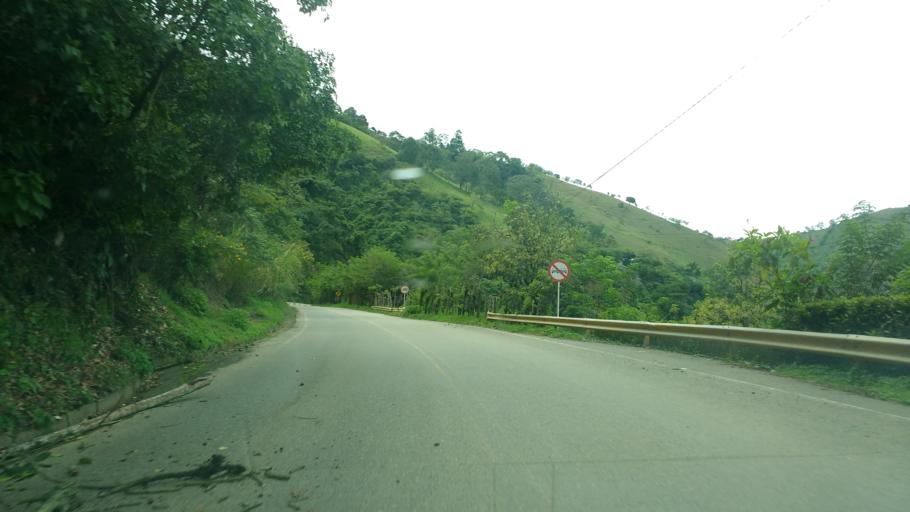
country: CO
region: Antioquia
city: Amaga
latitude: 6.0533
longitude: -75.7261
